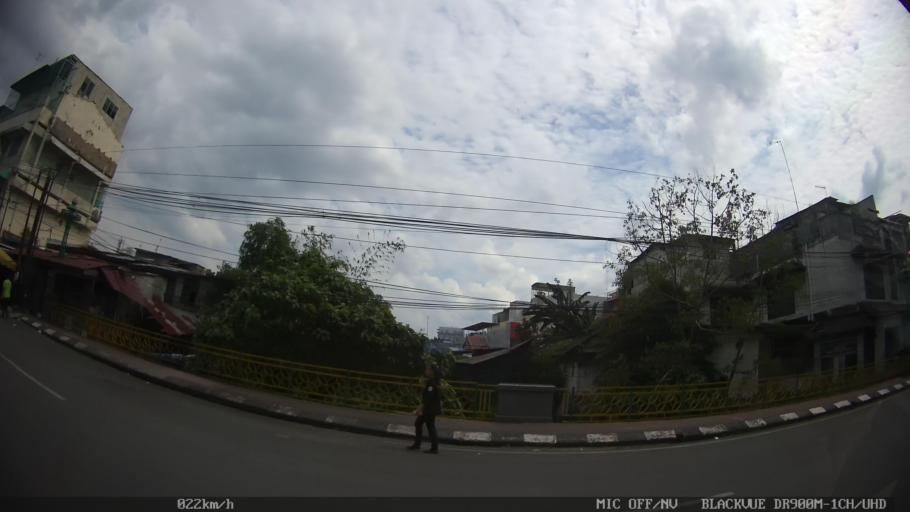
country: ID
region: North Sumatra
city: Medan
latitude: 3.5837
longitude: 98.6681
